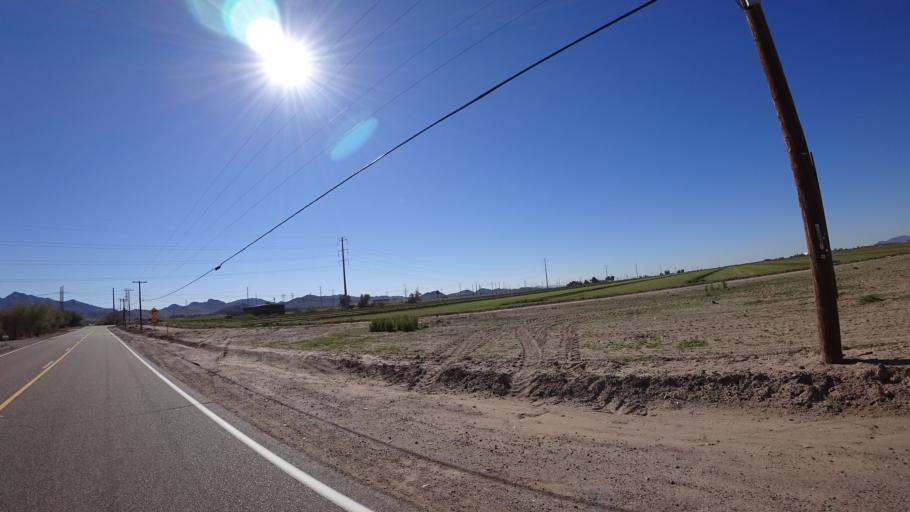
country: US
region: Arizona
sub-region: Maricopa County
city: Goodyear
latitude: 33.4086
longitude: -112.3575
